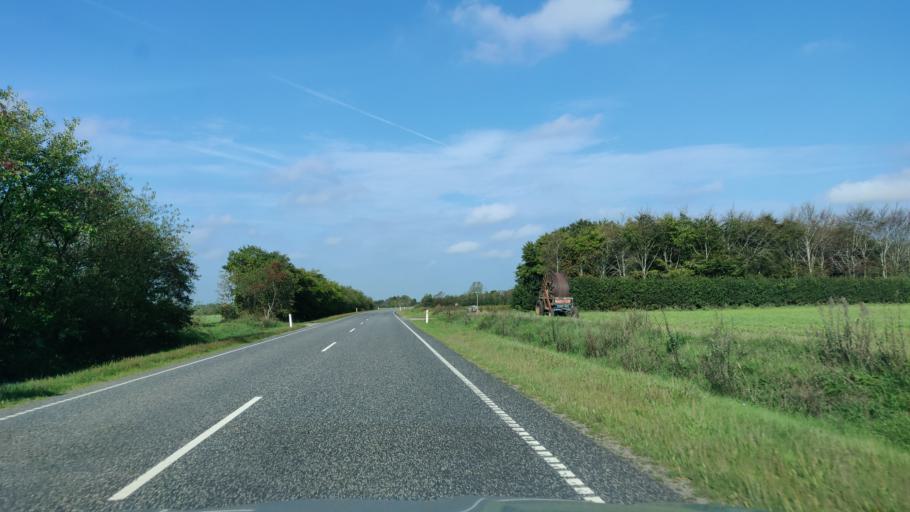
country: DK
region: Central Jutland
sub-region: Herning Kommune
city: Sunds
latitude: 56.2468
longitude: 9.0696
